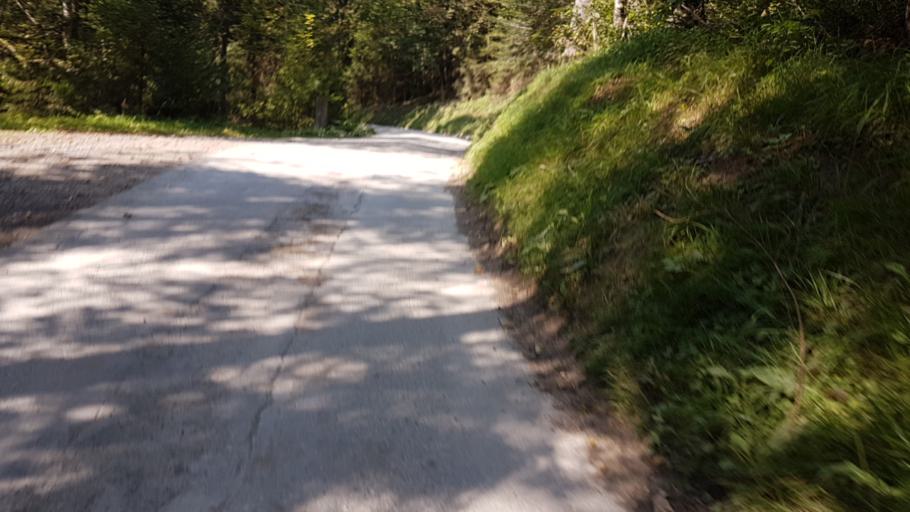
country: CH
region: Bern
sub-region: Frutigen-Niedersimmental District
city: Aeschi
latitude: 46.6280
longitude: 7.7506
